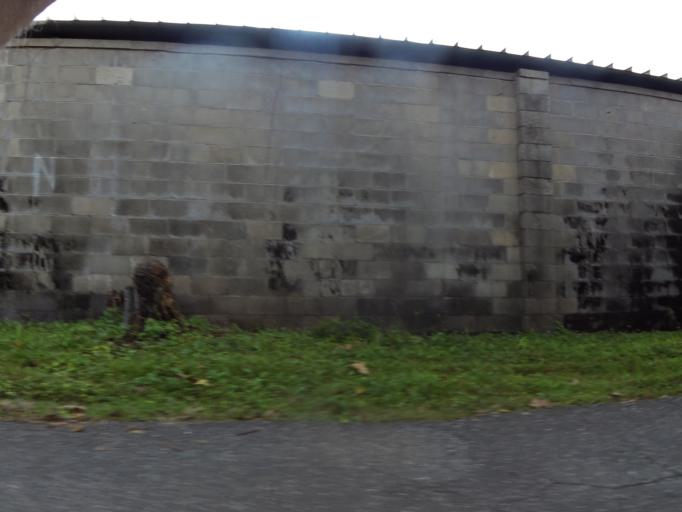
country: US
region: Florida
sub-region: Duval County
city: Jacksonville
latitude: 30.3207
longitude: -81.6981
